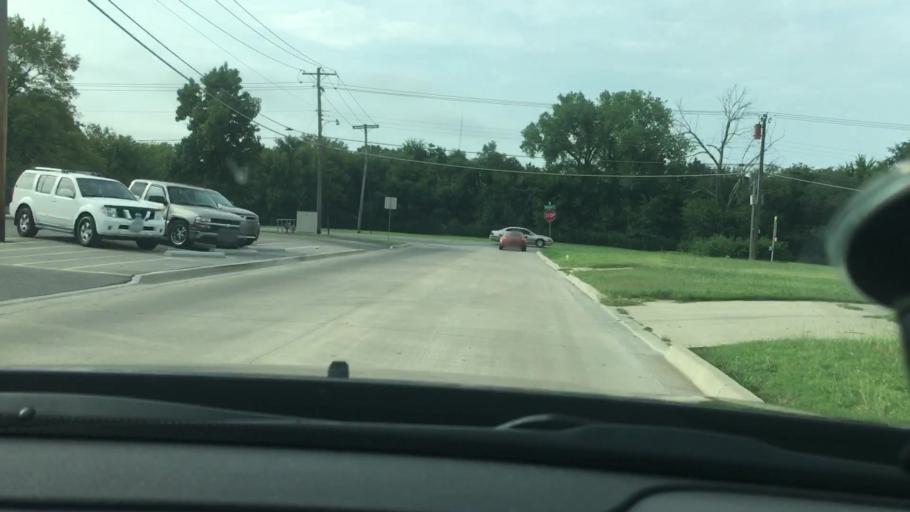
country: US
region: Oklahoma
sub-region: Carter County
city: Ardmore
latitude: 34.1880
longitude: -97.1255
